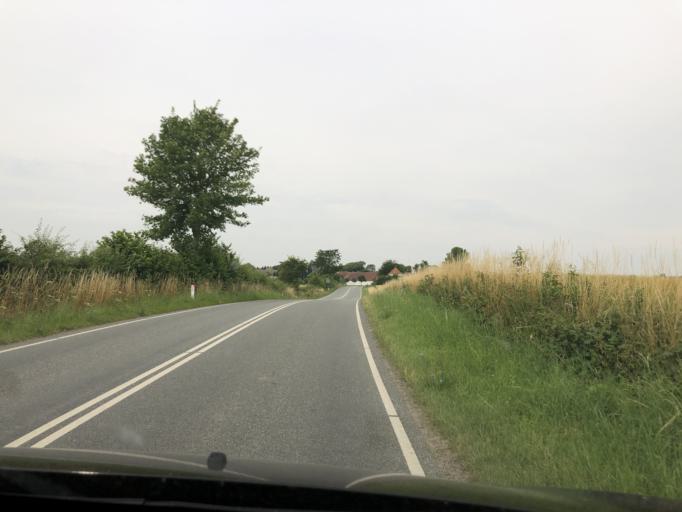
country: DK
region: South Denmark
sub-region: Assens Kommune
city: Glamsbjerg
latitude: 55.2919
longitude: 10.0799
